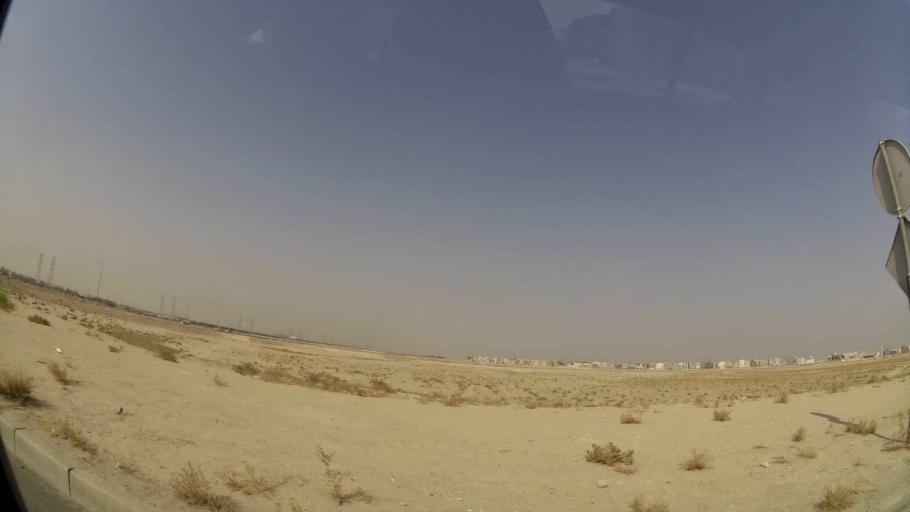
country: KW
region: Muhafazat al Jahra'
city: Al Jahra'
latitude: 29.3345
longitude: 47.7577
